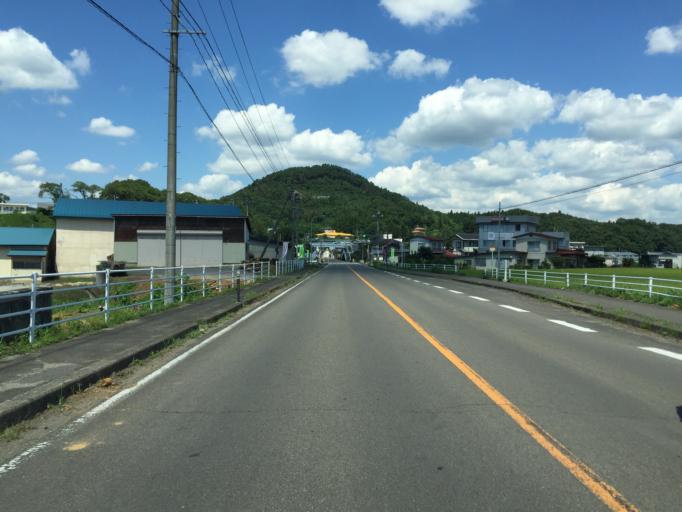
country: JP
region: Fukushima
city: Nihommatsu
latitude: 37.6322
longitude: 140.4629
